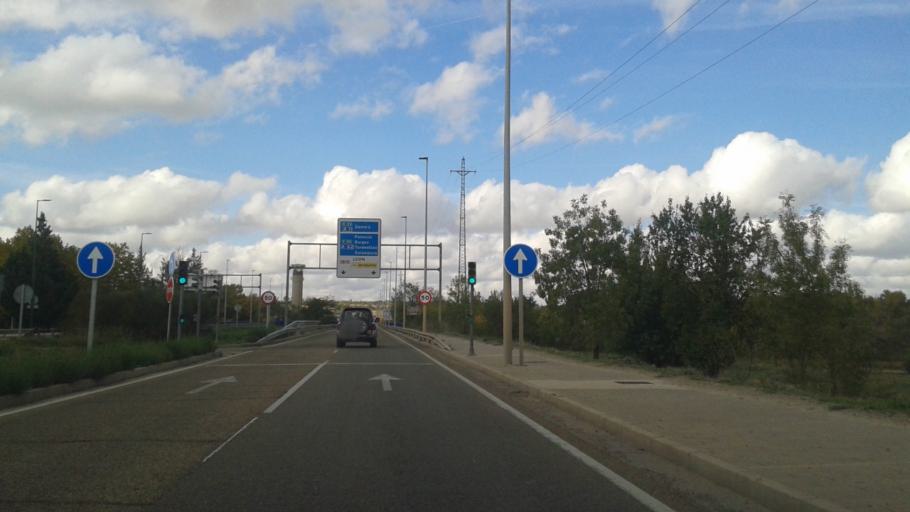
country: ES
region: Castille and Leon
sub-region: Provincia de Valladolid
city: Valladolid
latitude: 41.6720
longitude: -4.7105
